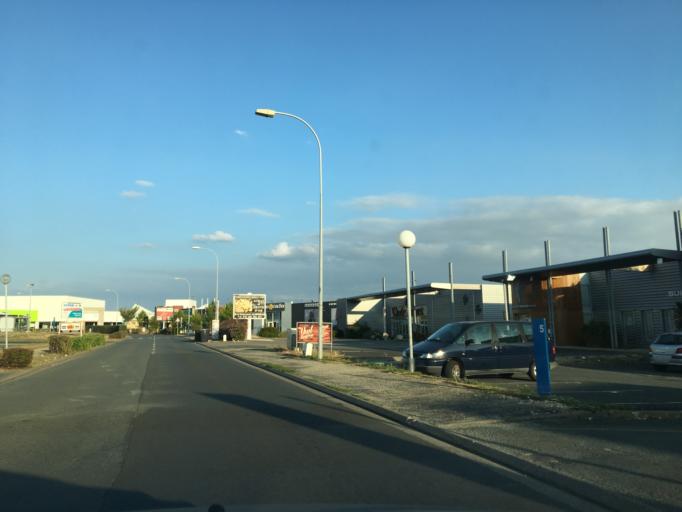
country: FR
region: Poitou-Charentes
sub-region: Departement de la Charente-Maritime
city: Angoulins
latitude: 46.1051
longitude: -1.1001
